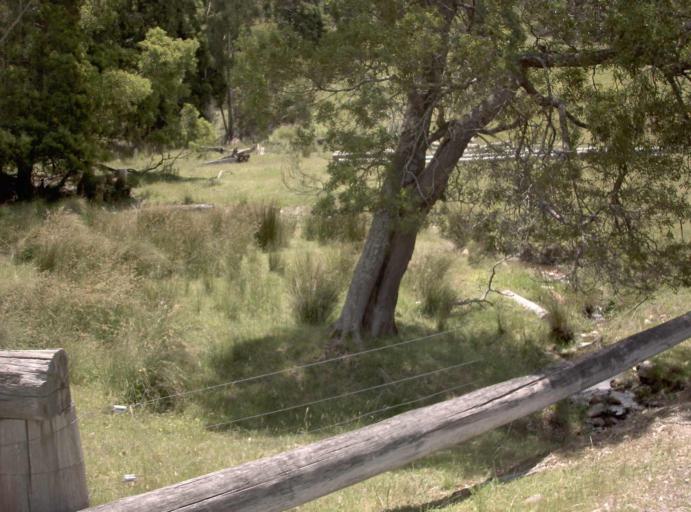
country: AU
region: New South Wales
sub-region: Bombala
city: Bombala
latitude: -37.3660
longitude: 149.0178
